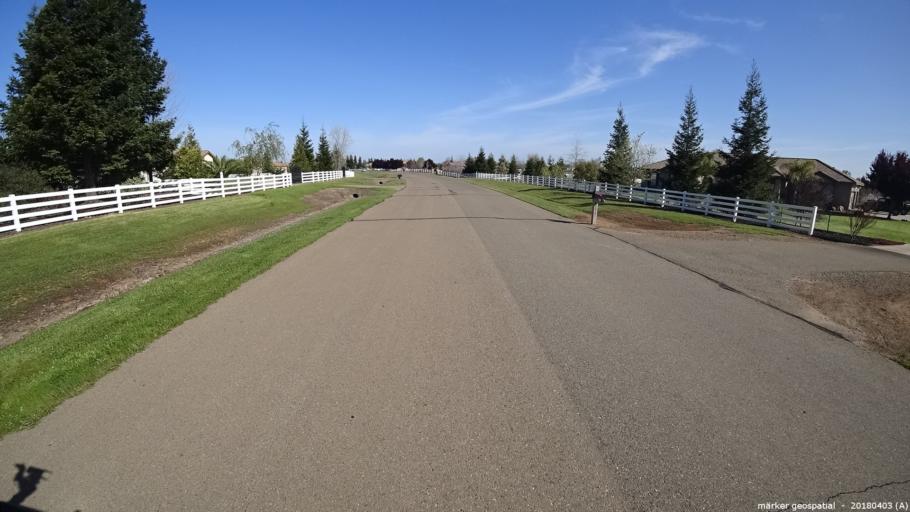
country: US
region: California
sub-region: Sacramento County
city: Clay
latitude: 38.4127
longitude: -121.1881
